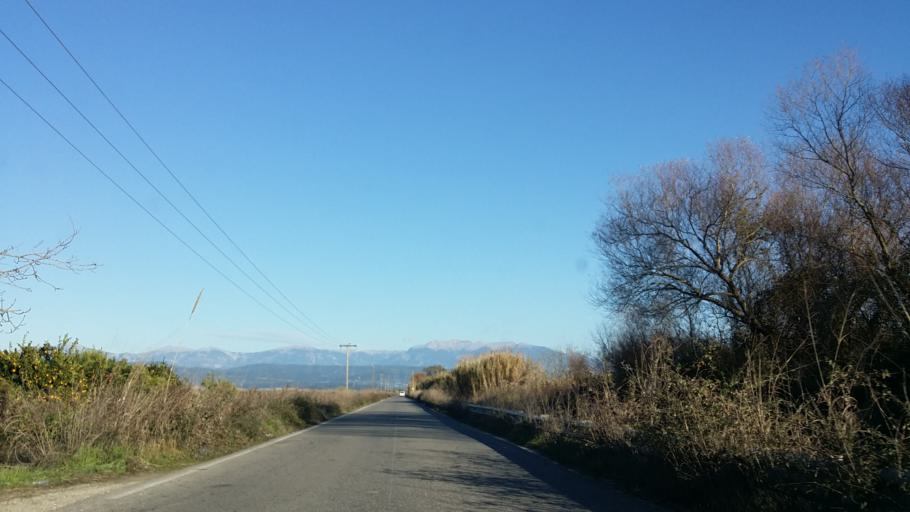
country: GR
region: West Greece
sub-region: Nomos Aitolias kai Akarnanias
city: Lepenou
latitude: 38.6439
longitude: 21.2644
